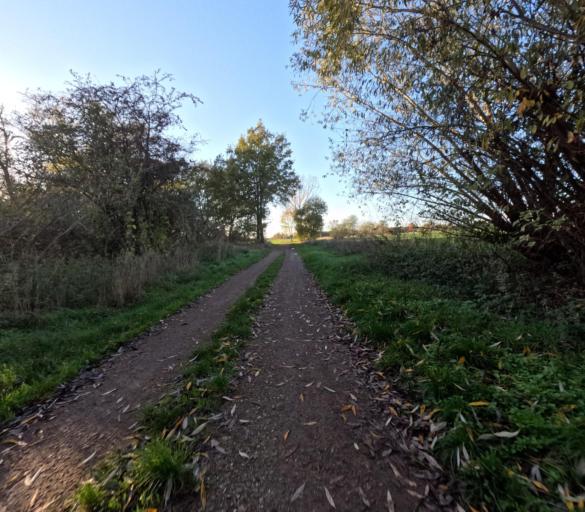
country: DE
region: Saxony-Anhalt
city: Zoschen
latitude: 51.3641
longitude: 12.1157
